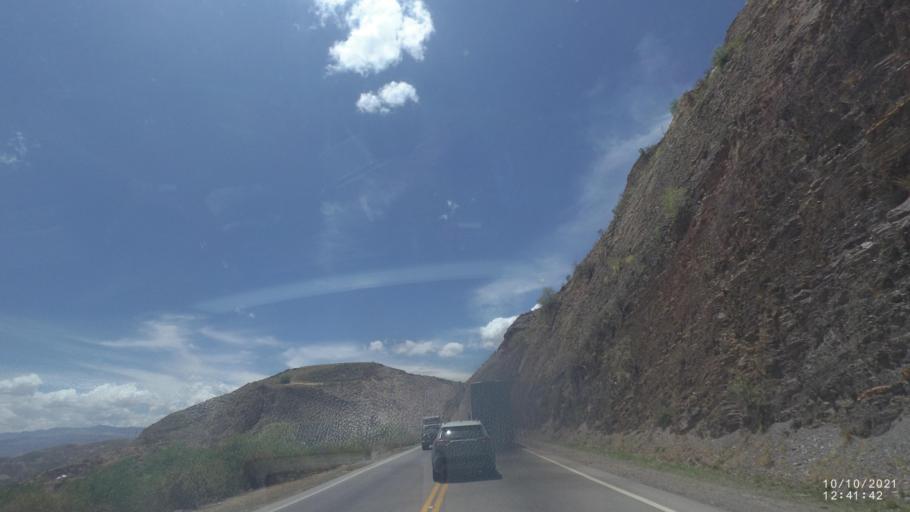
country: BO
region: Cochabamba
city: Irpa Irpa
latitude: -17.6341
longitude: -66.3907
